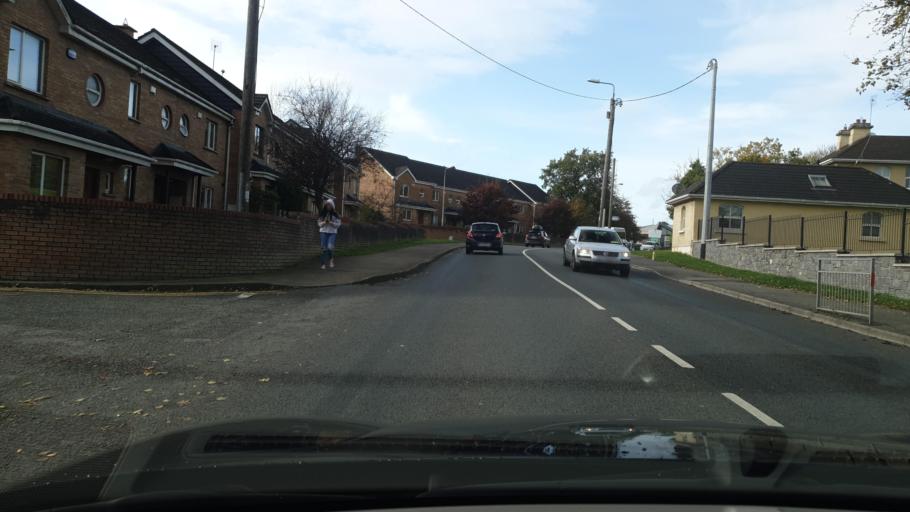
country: IE
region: Leinster
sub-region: An Mhi
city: Ratoath
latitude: 53.5056
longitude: -6.4555
